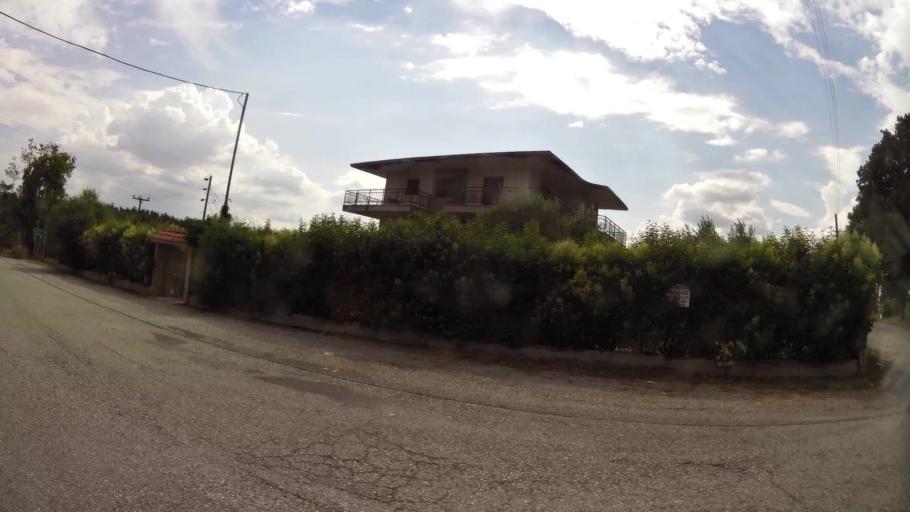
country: GR
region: Central Macedonia
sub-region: Nomos Pierias
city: Makrygialos
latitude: 40.4162
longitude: 22.5955
